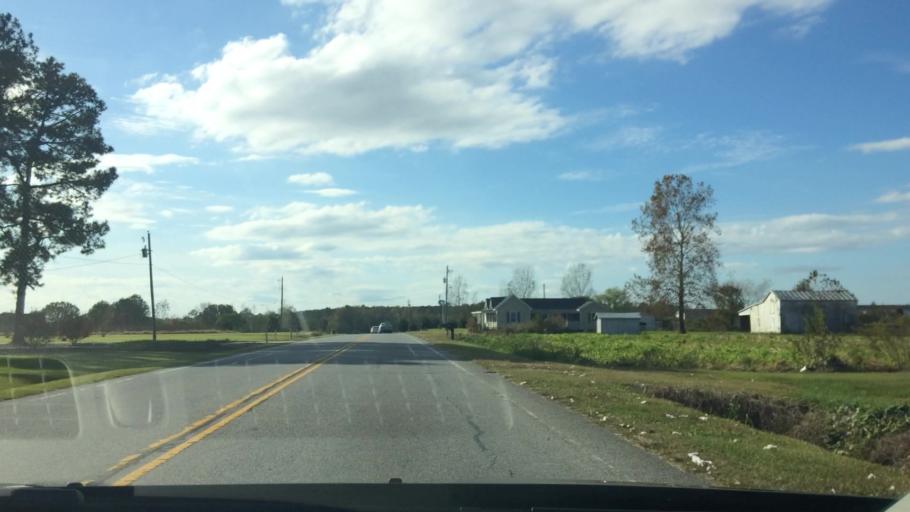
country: US
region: North Carolina
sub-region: Greene County
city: Snow Hill
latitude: 35.4420
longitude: -77.8082
